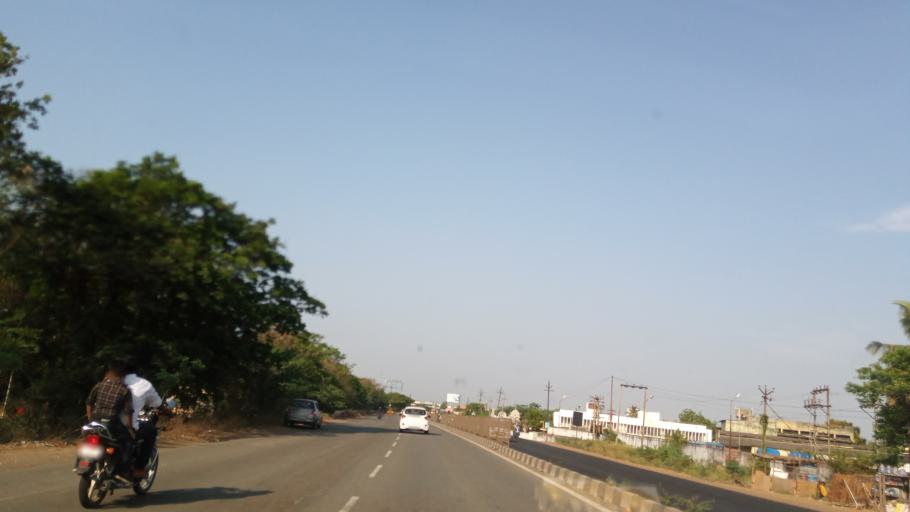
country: IN
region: Tamil Nadu
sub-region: Kancheepuram
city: Poonamalle
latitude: 13.0418
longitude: 80.0603
